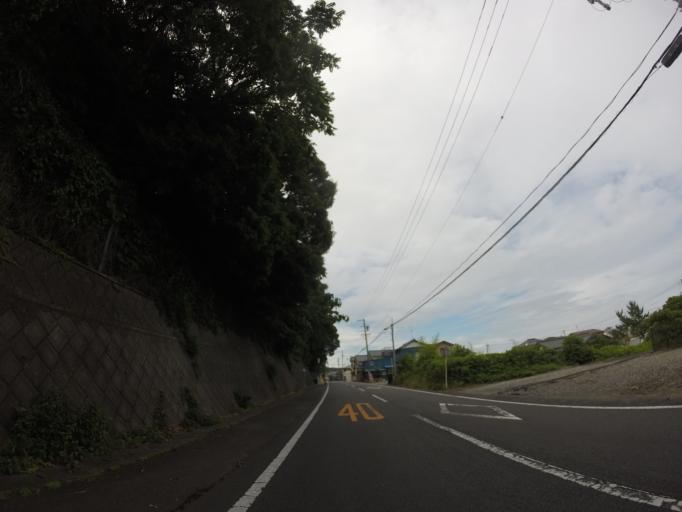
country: JP
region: Shizuoka
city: Oyama
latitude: 34.6289
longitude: 138.1972
